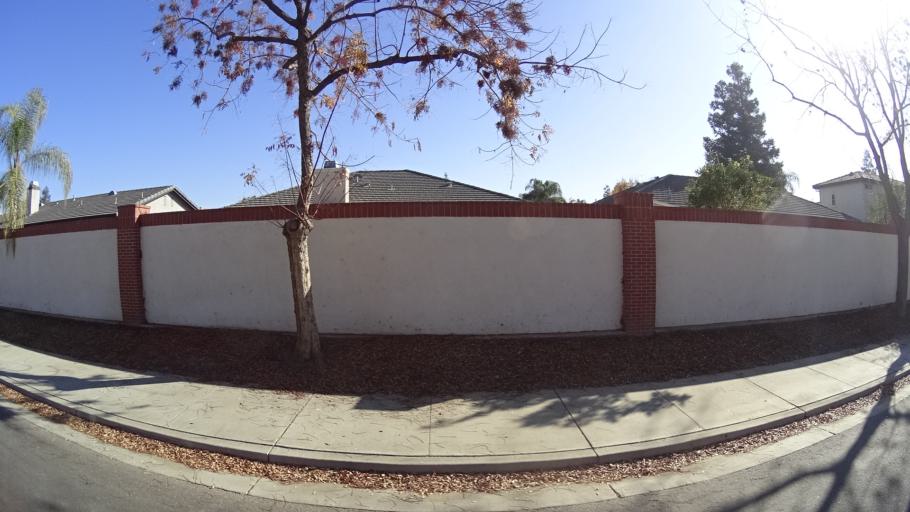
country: US
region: California
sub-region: Kern County
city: Rosedale
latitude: 35.3282
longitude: -119.1329
